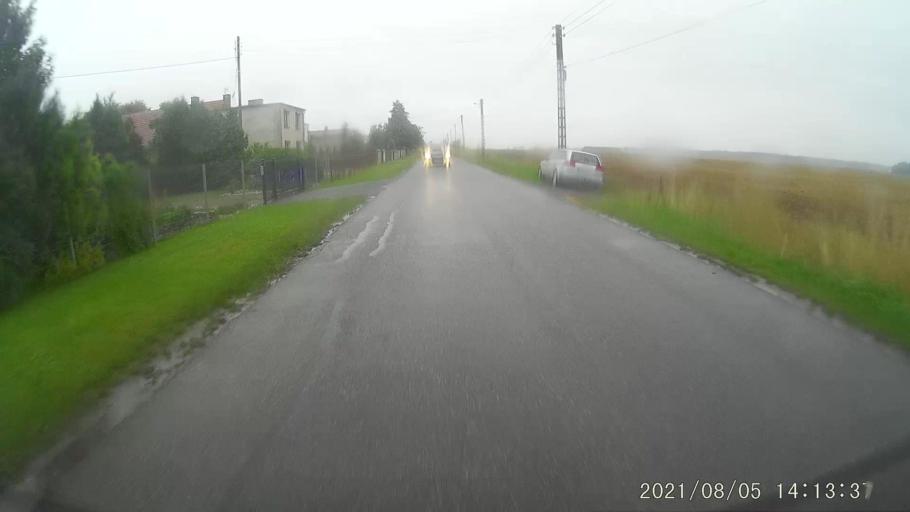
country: PL
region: Opole Voivodeship
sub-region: Powiat krapkowicki
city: Strzeleczki
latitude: 50.4706
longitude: 17.7451
